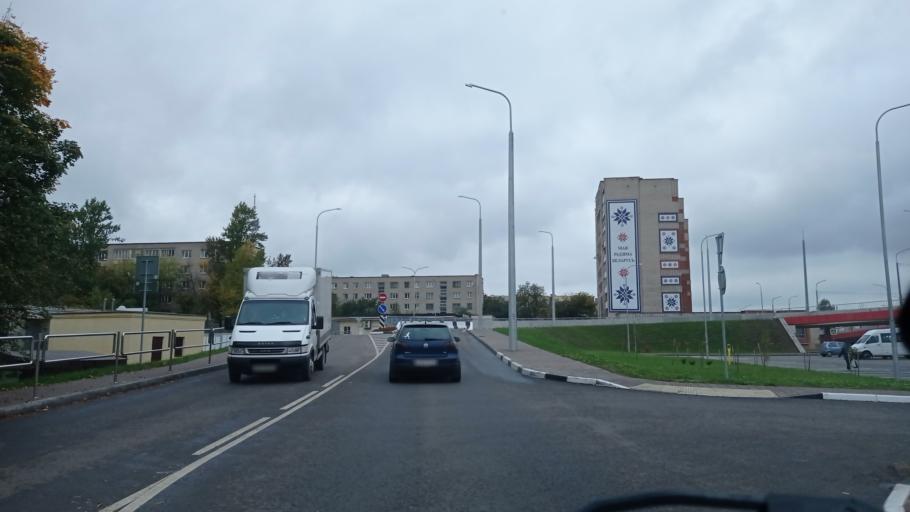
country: BY
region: Vitebsk
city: Vitebsk
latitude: 55.1981
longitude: 30.1846
